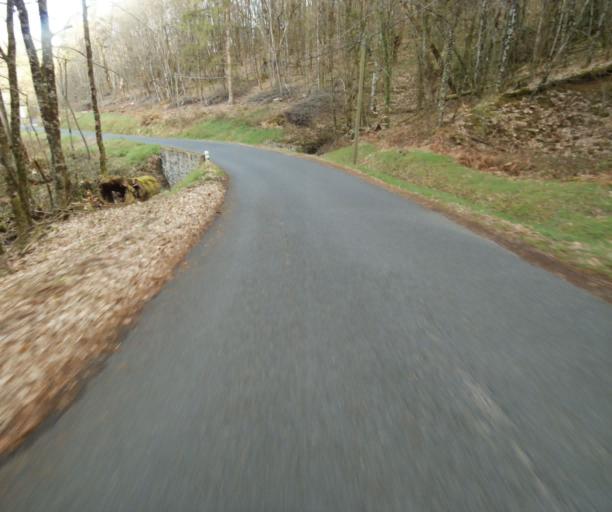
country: FR
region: Limousin
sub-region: Departement de la Correze
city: Correze
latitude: 45.3403
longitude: 1.8235
